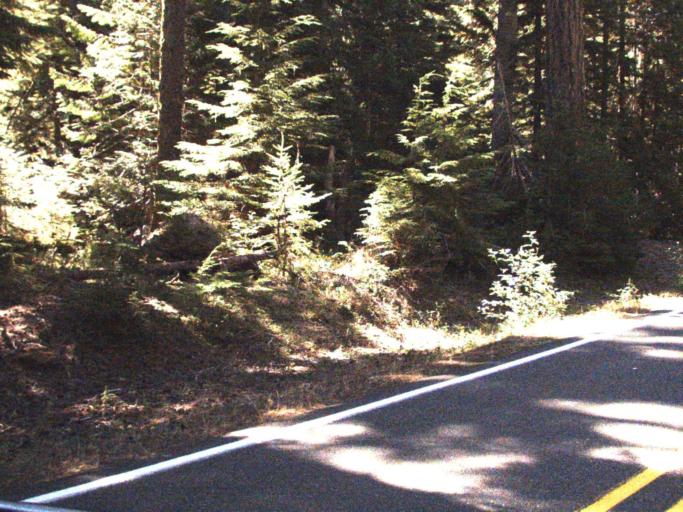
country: US
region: Washington
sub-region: King County
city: Enumclaw
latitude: 46.9762
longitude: -121.5364
